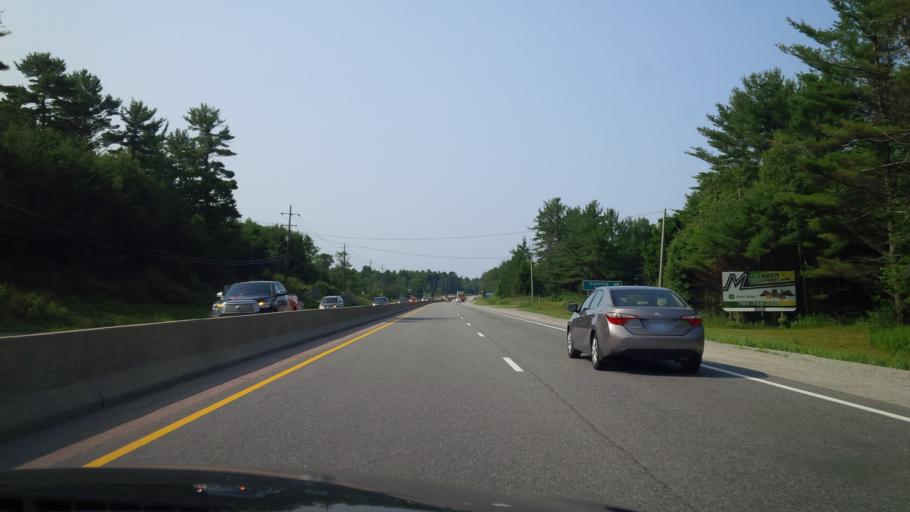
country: CA
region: Ontario
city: Gravenhurst
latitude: 44.8072
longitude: -79.3275
